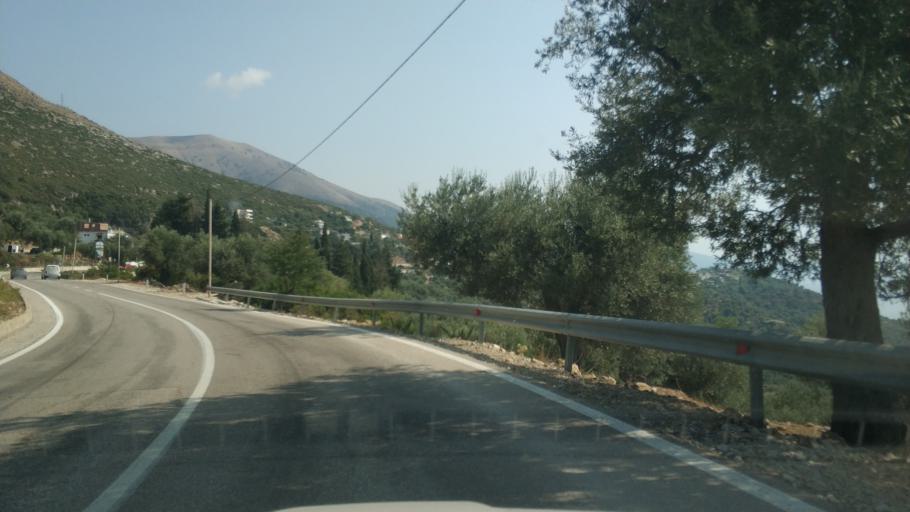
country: AL
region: Vlore
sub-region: Rrethi i Sarandes
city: Lukove
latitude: 40.0229
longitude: 19.8866
